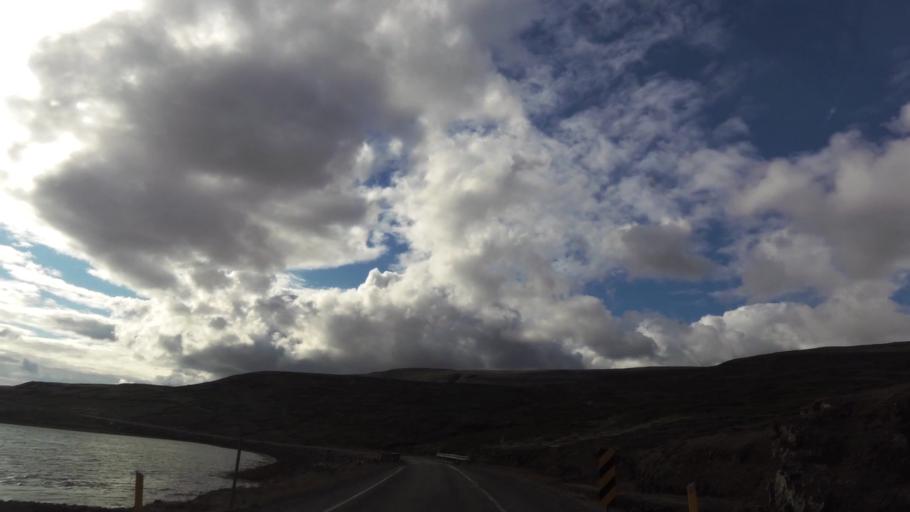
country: IS
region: West
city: Olafsvik
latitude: 65.5371
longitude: -23.7883
